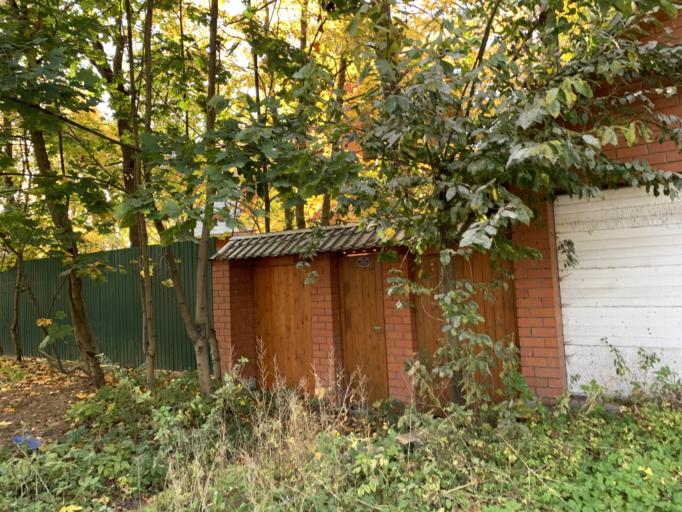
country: RU
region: Moskovskaya
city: Mamontovka
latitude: 55.9903
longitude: 37.8338
